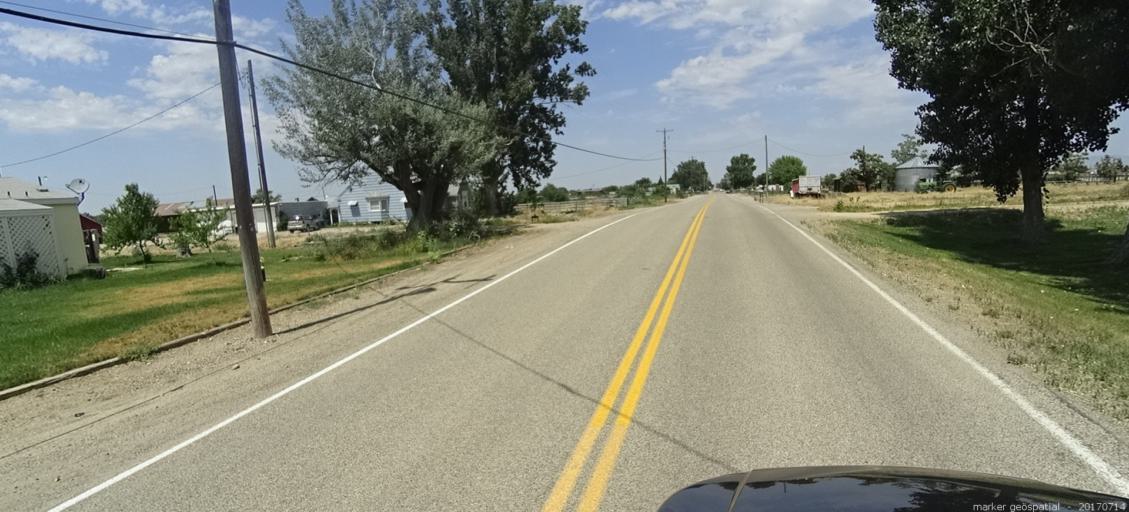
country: US
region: Idaho
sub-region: Ada County
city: Kuna
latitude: 43.5278
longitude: -116.3543
